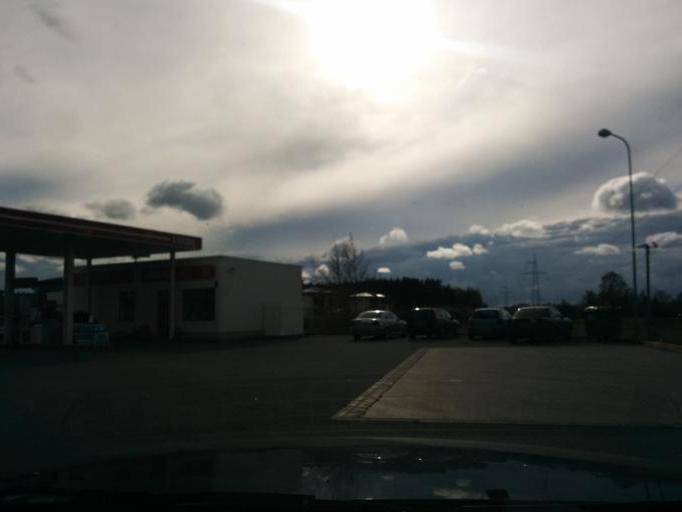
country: LV
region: Jelgava
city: Jelgava
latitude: 56.6245
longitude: 23.7242
